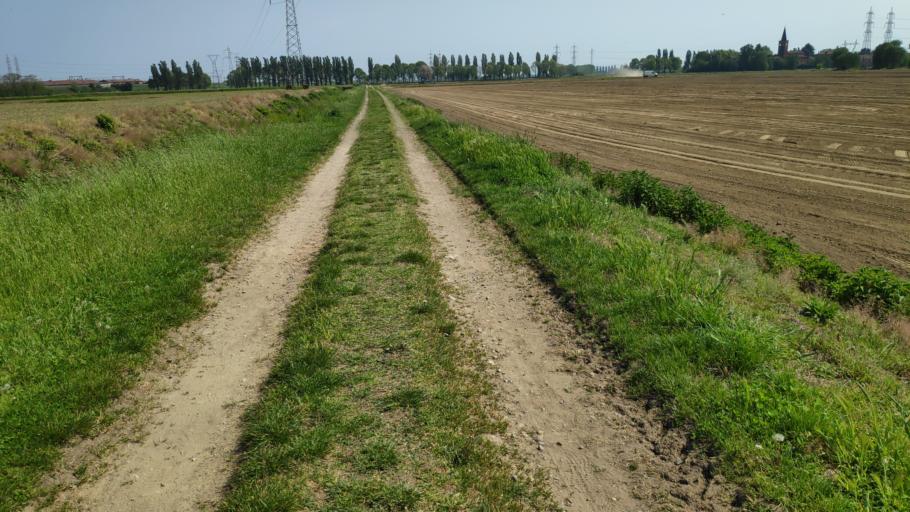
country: IT
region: Lombardy
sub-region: Citta metropolitana di Milano
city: Civesio
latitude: 45.3933
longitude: 9.2762
